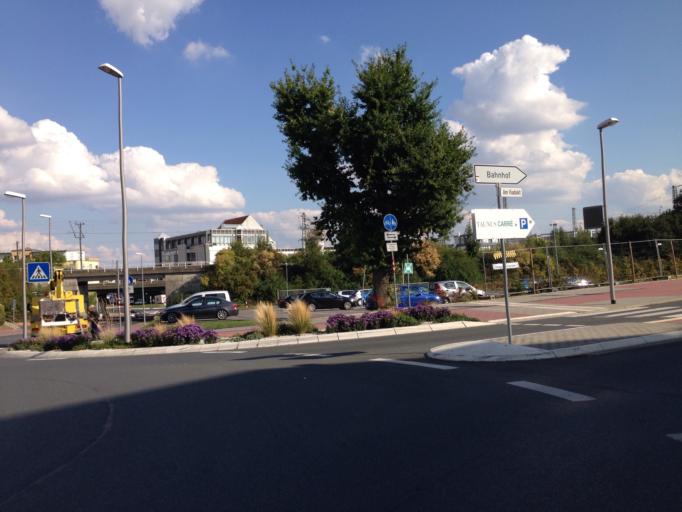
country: DE
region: Hesse
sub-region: Regierungsbezirk Darmstadt
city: Friedrichsdorf
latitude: 50.2558
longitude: 8.6431
